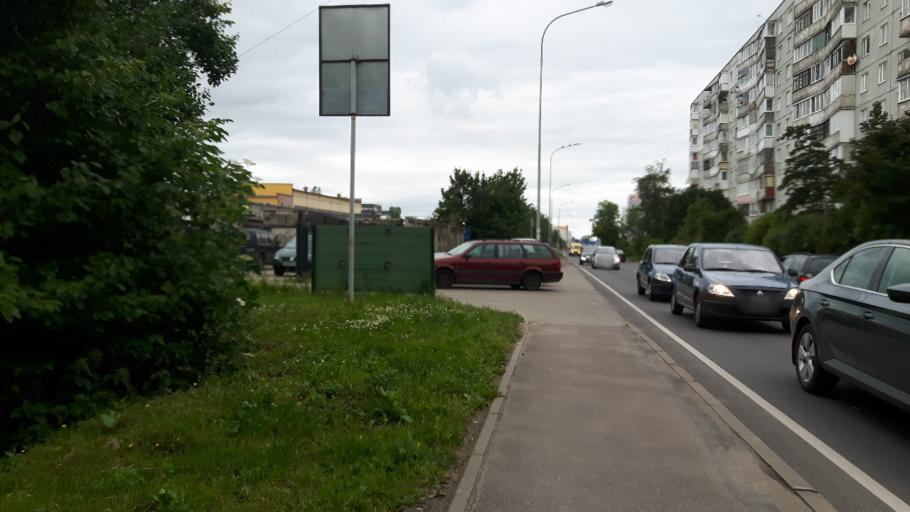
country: RU
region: Kaliningrad
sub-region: Gorod Kaliningrad
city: Kaliningrad
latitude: 54.7361
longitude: 20.4970
